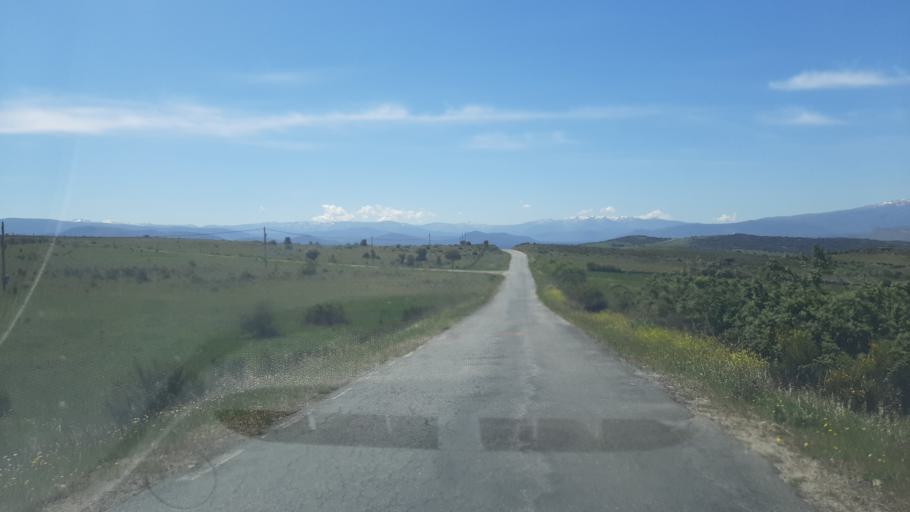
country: ES
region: Castille and Leon
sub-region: Provincia de Avila
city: Narrillos del Alamo
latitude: 40.5609
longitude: -5.4394
